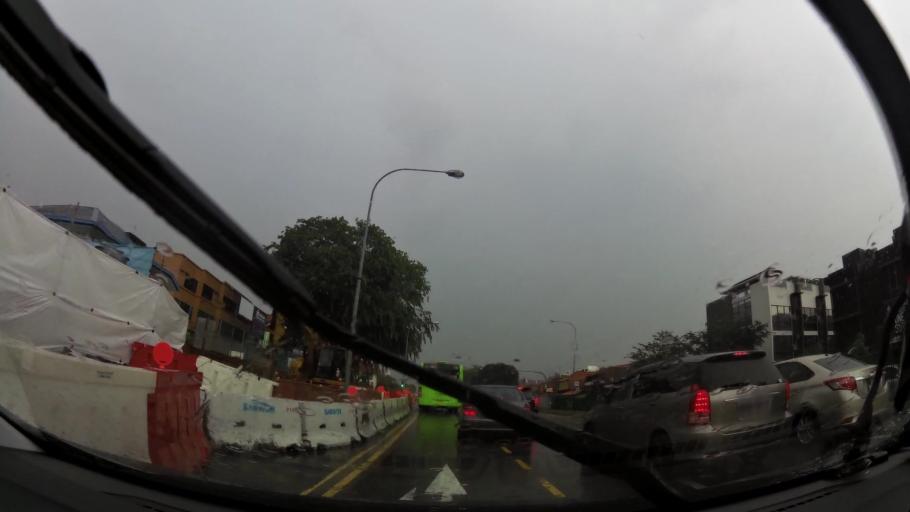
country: SG
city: Singapore
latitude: 1.3550
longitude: 103.8792
